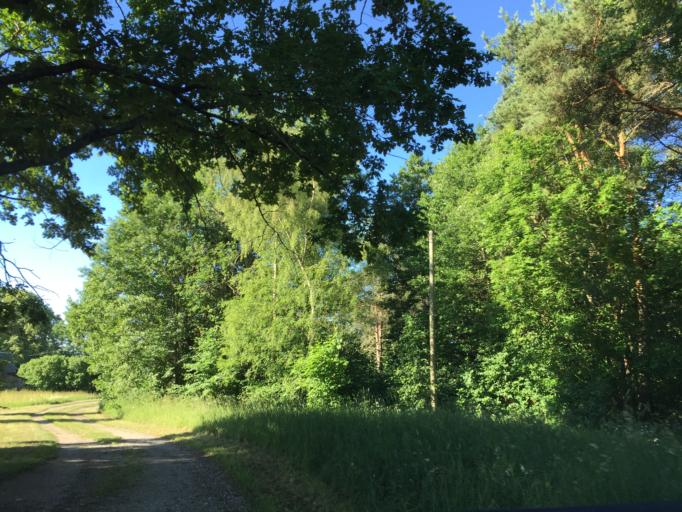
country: LV
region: Ventspils
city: Ventspils
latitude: 57.4102
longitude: 21.6460
